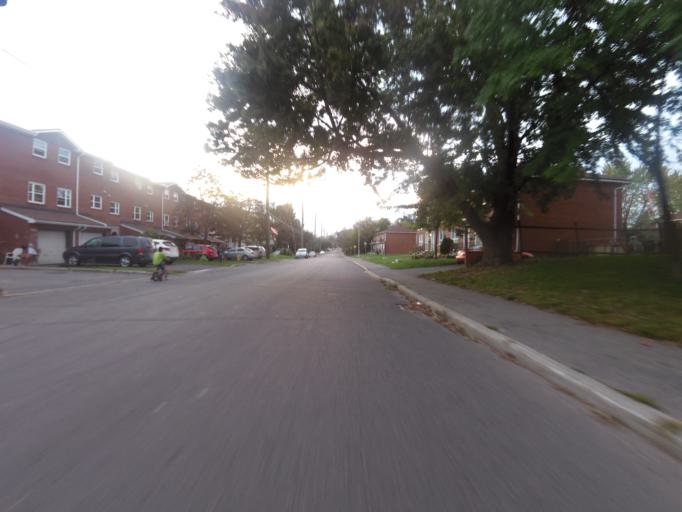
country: CA
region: Ontario
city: Ottawa
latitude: 45.4230
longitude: -75.6565
